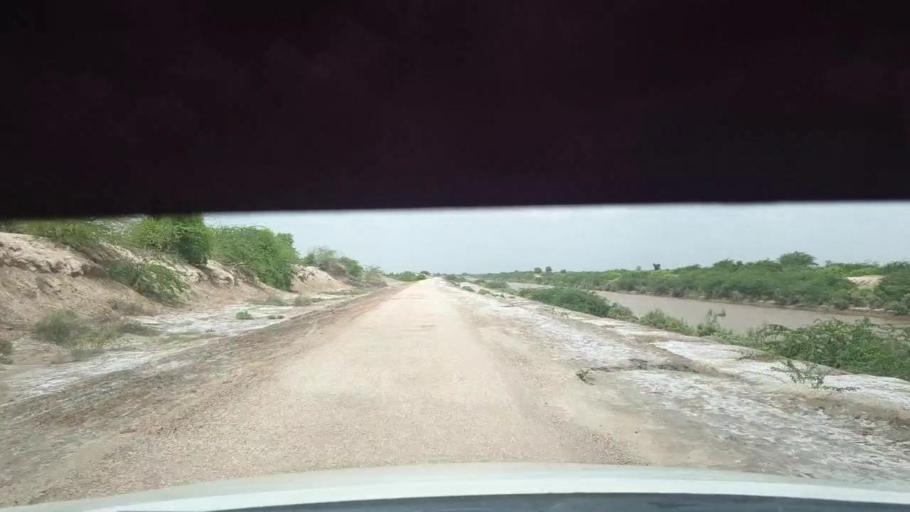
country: PK
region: Sindh
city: Kadhan
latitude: 24.5124
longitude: 69.1196
